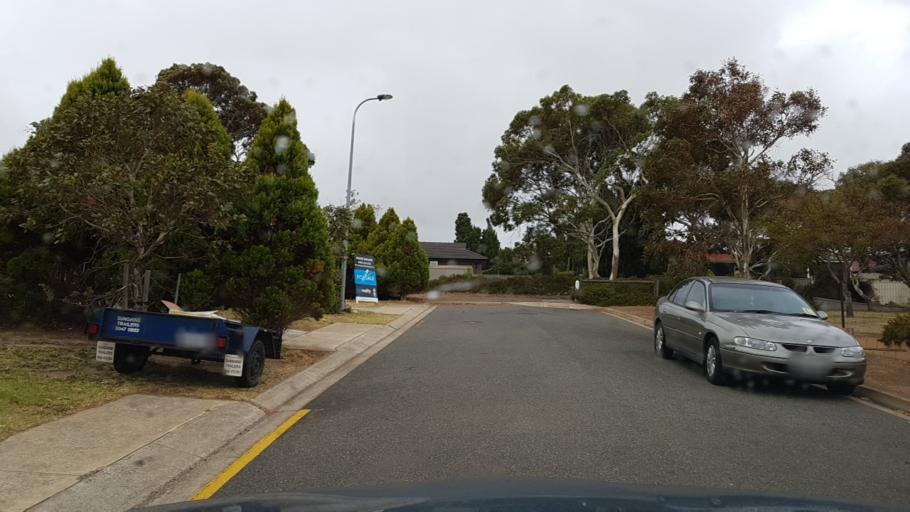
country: AU
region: South Australia
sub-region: Onkaparinga
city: Moana
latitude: -35.2021
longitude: 138.4855
